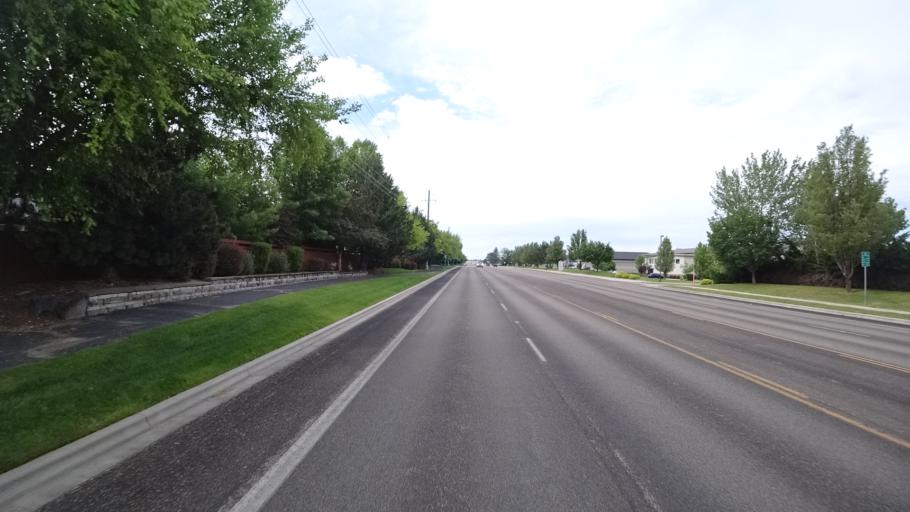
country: US
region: Idaho
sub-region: Ada County
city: Meridian
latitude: 43.6009
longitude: -116.3745
